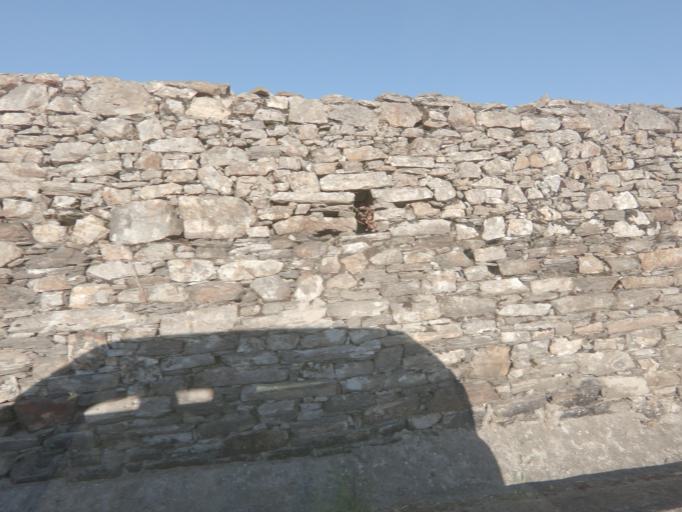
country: PT
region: Vila Real
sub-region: Peso da Regua
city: Godim
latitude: 41.1618
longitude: -7.8176
